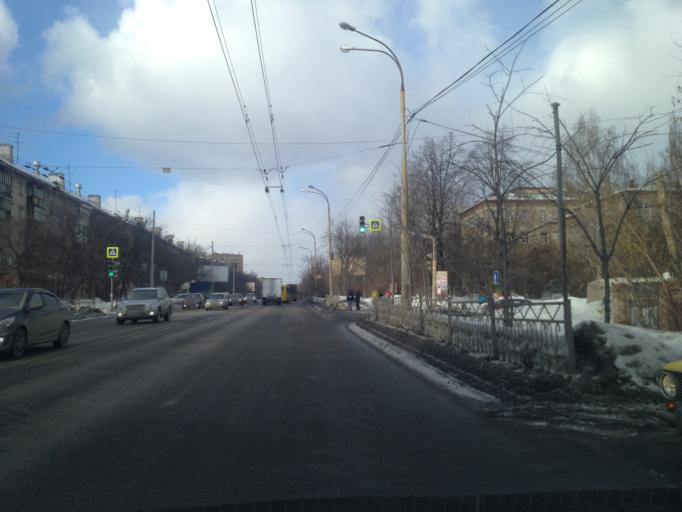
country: RU
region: Sverdlovsk
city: Yekaterinburg
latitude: 56.8525
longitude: 60.6555
